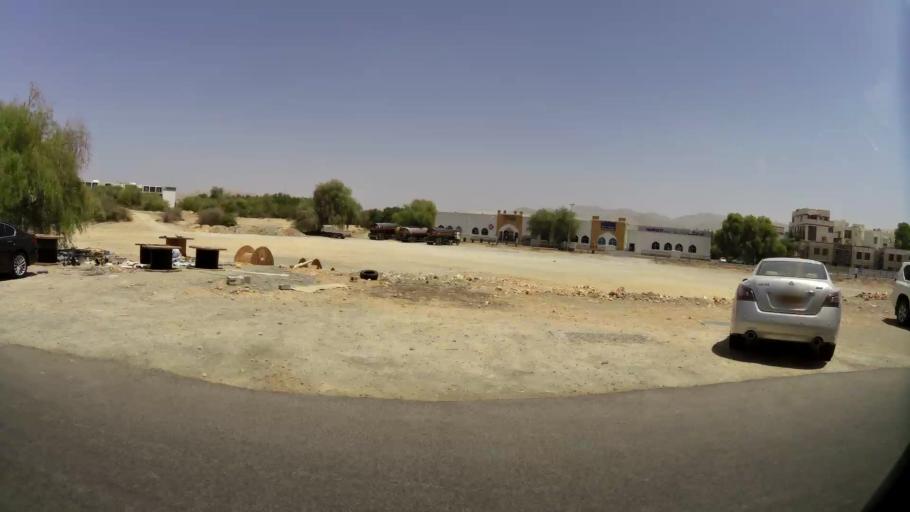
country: OM
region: Muhafazat Masqat
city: Muscat
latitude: 23.6239
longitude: 58.4884
